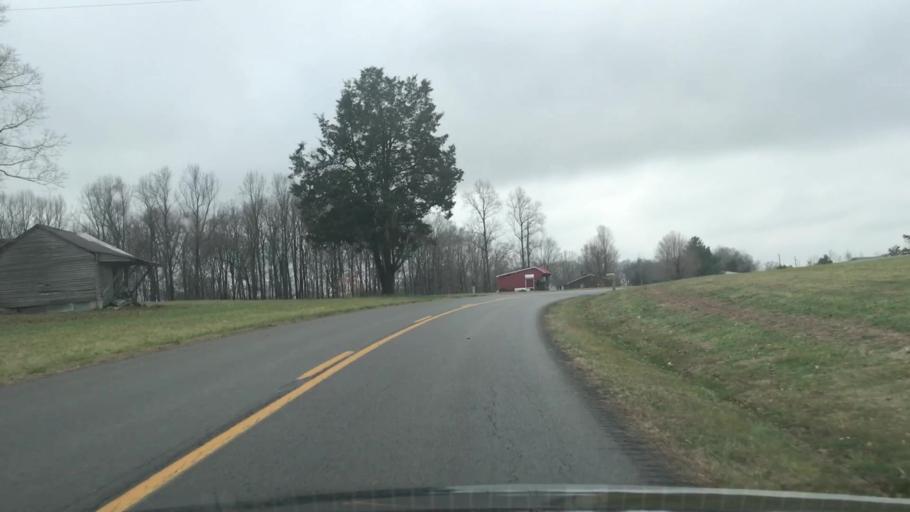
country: US
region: Kentucky
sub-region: Monroe County
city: Tompkinsville
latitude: 36.7848
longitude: -85.7400
